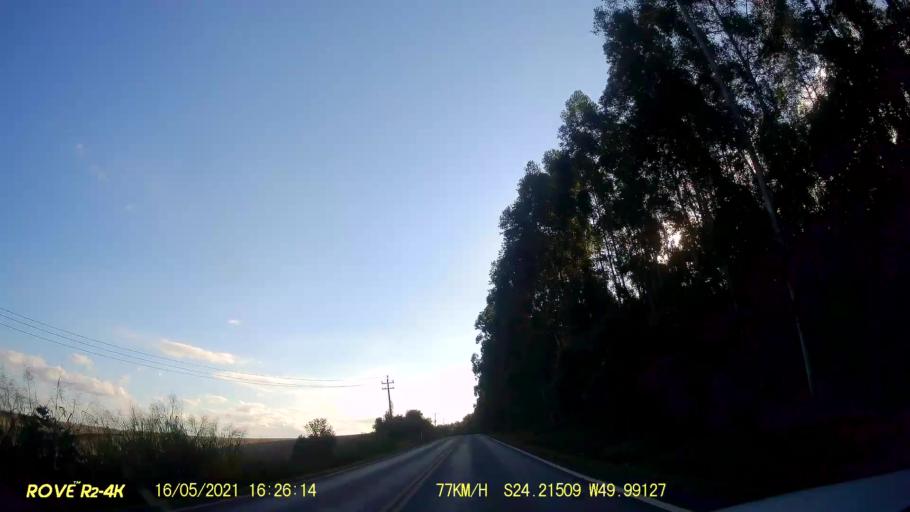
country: BR
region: Parana
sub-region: Jaguariaiva
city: Jaguariaiva
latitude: -24.2151
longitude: -49.9914
